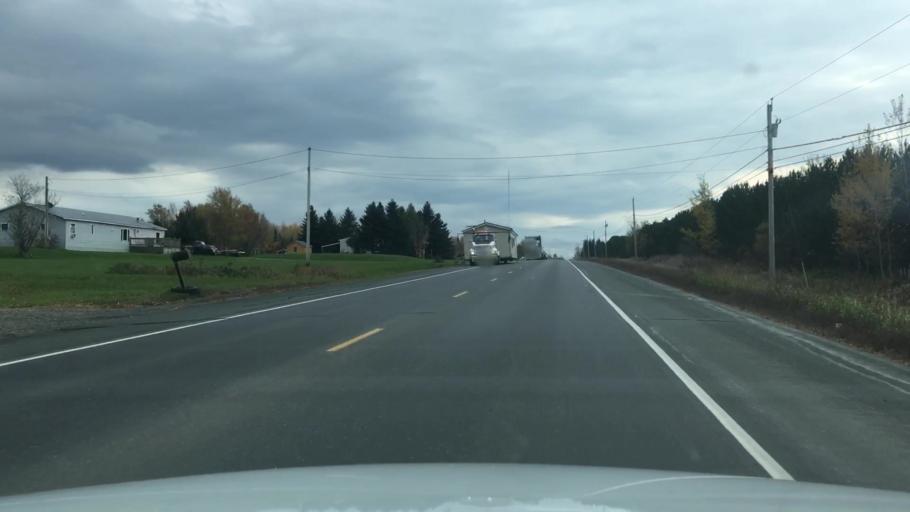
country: US
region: Maine
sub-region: Aroostook County
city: Caribou
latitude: 46.7752
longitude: -67.9894
